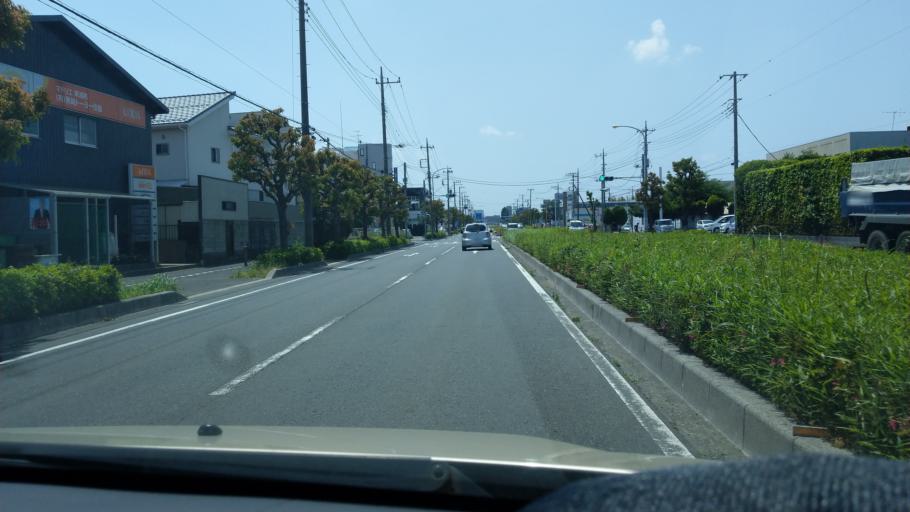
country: JP
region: Saitama
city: Saitama
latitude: 35.8783
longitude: 139.6878
